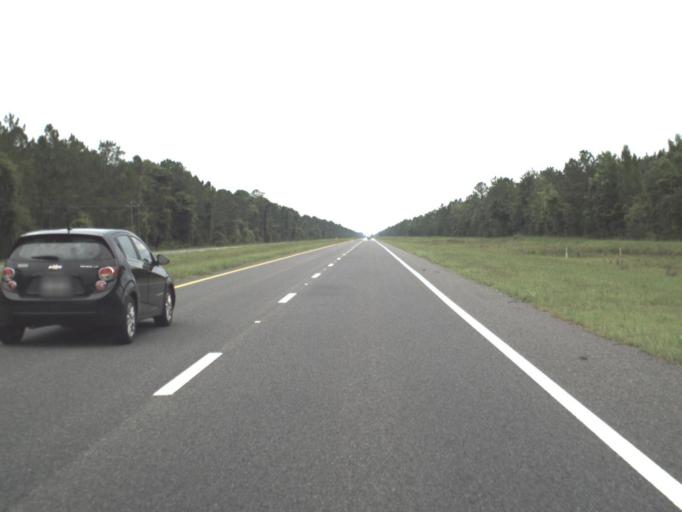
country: US
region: Florida
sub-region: Levy County
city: Chiefland
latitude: 29.3614
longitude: -82.7892
